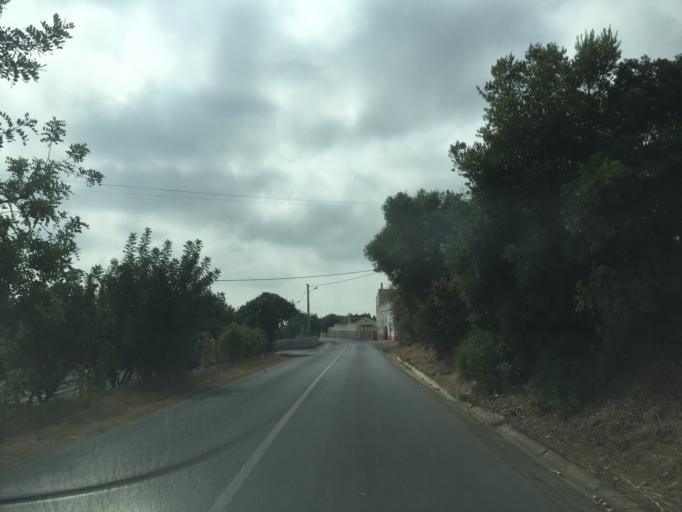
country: PT
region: Faro
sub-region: Olhao
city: Olhao
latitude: 37.0732
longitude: -7.8866
